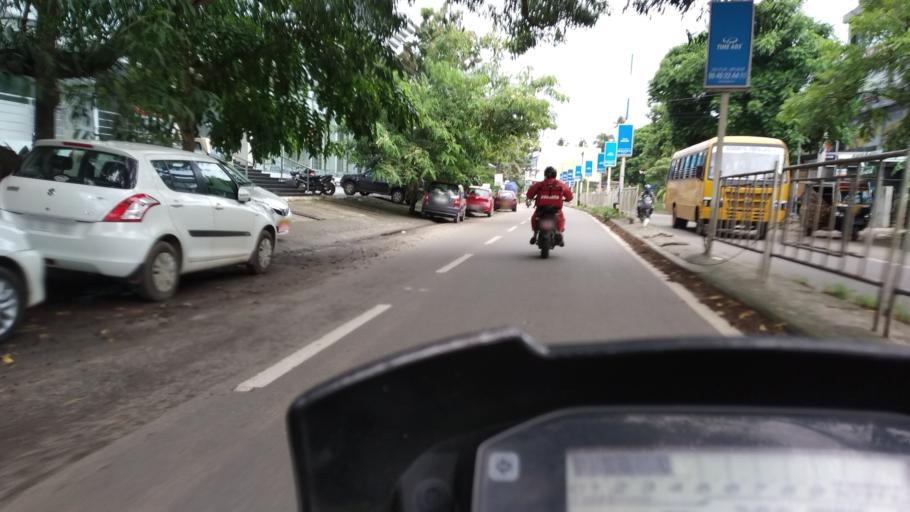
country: IN
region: Kerala
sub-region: Ernakulam
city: Cochin
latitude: 9.9874
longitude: 76.2958
